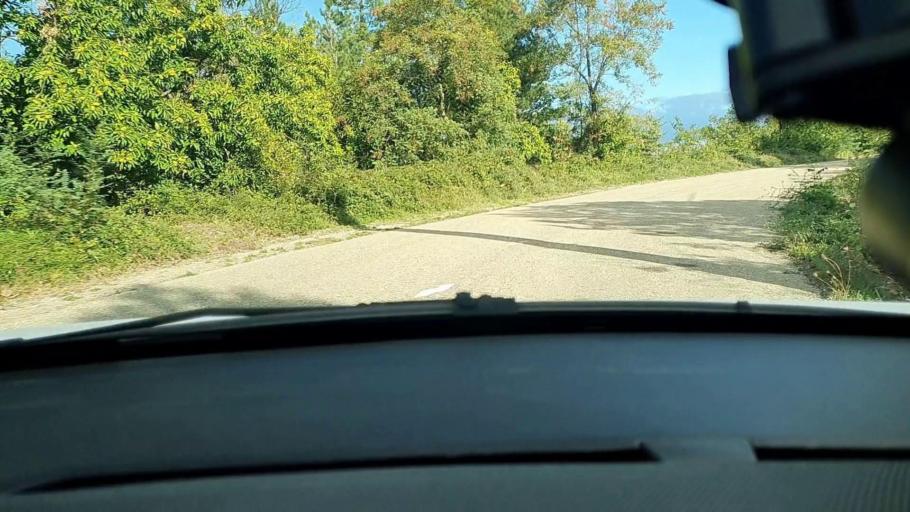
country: FR
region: Rhone-Alpes
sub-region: Departement de l'Ardeche
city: Les Vans
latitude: 44.3916
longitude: 3.9912
